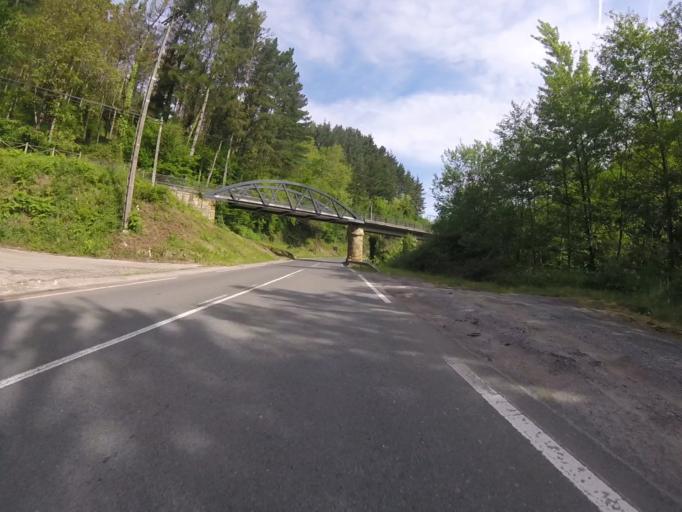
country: ES
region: Basque Country
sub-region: Provincia de Guipuzcoa
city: Azkoitia
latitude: 43.1638
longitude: -2.3311
